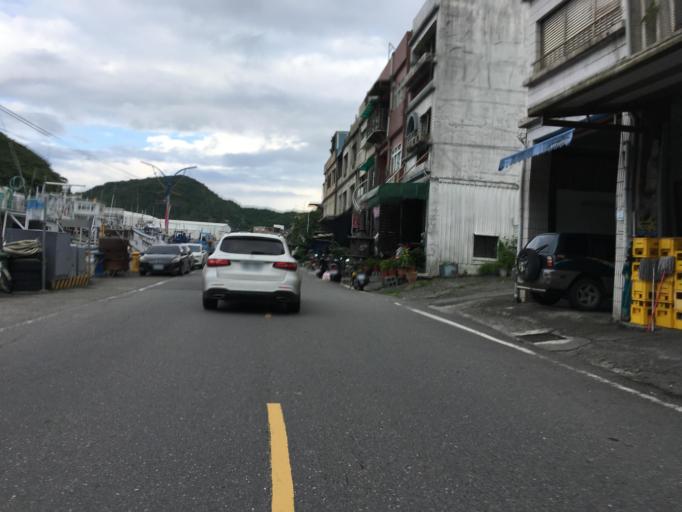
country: TW
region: Taiwan
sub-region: Yilan
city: Yilan
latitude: 24.5774
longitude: 121.8688
